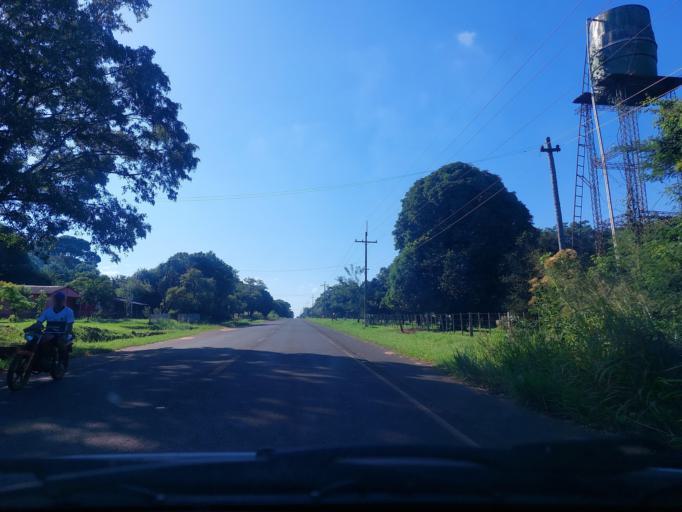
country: PY
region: San Pedro
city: Guayaybi
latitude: -24.5317
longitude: -56.4702
